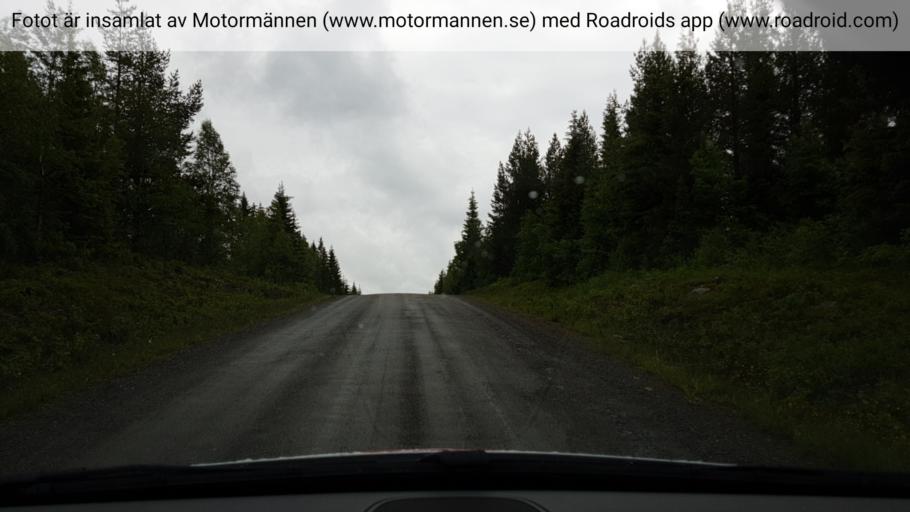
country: SE
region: Jaemtland
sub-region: Stroemsunds Kommun
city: Stroemsund
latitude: 64.2545
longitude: 15.0240
